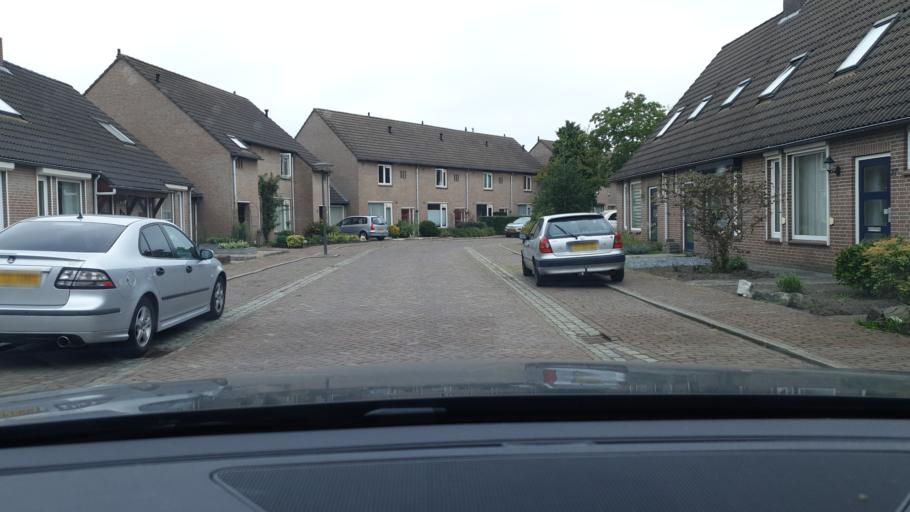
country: NL
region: North Brabant
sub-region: Gemeente Landerd
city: Schaijk
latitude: 51.7433
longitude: 5.6270
